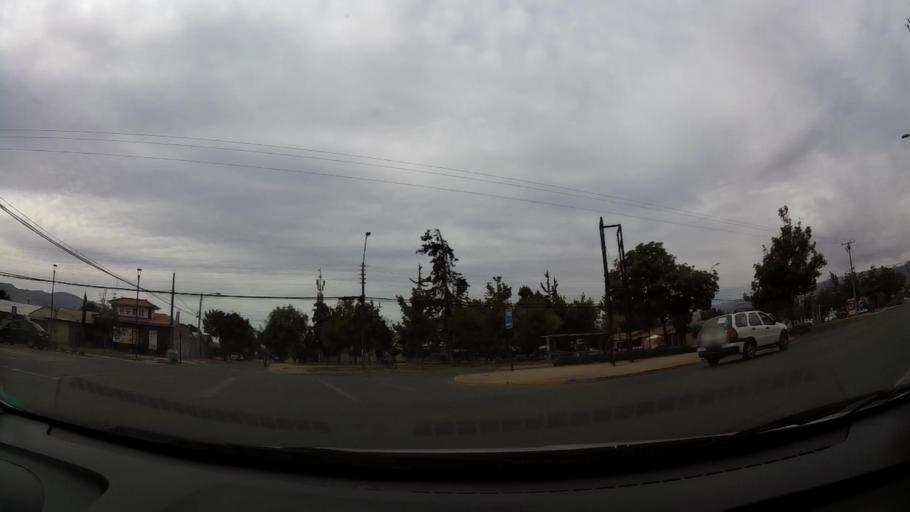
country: CL
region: O'Higgins
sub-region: Provincia de Cachapoal
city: Rancagua
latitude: -34.1548
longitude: -70.7406
